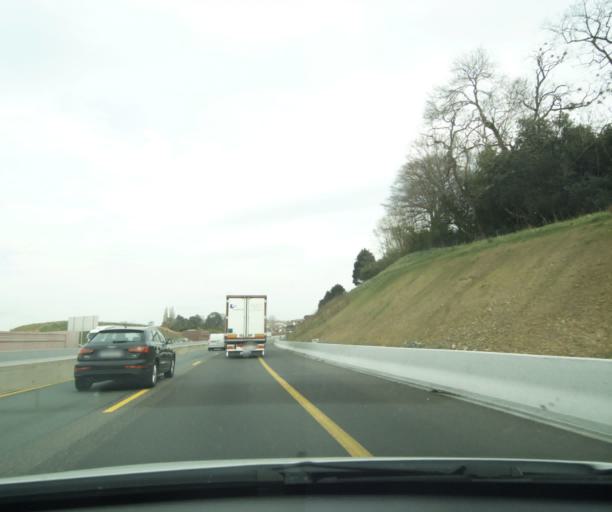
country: FR
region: Aquitaine
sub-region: Departement des Pyrenees-Atlantiques
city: Ciboure
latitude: 43.3748
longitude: -1.6670
